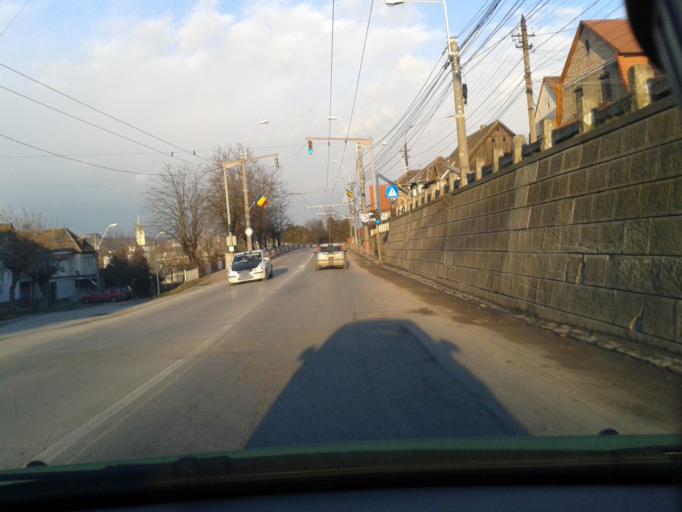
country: RO
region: Sibiu
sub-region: Municipiul Medias
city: Medias
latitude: 46.1579
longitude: 24.3454
